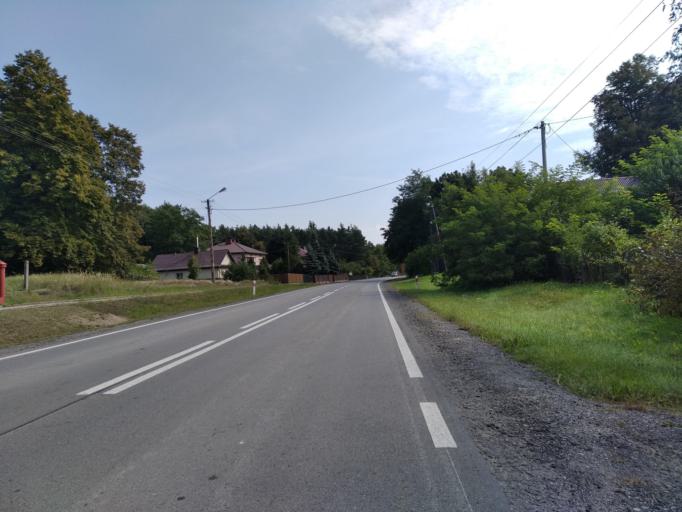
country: PL
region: Subcarpathian Voivodeship
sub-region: Powiat mielecki
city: Przeclaw
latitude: 50.1581
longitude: 21.5447
